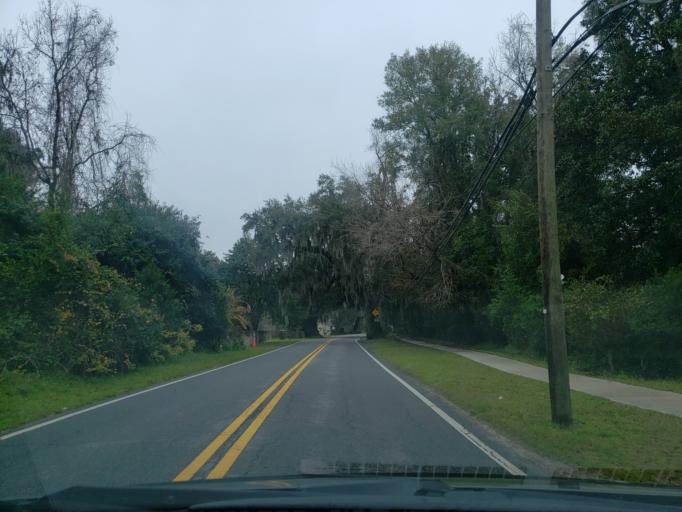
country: US
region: Georgia
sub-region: Chatham County
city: Montgomery
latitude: 31.9440
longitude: -81.1485
